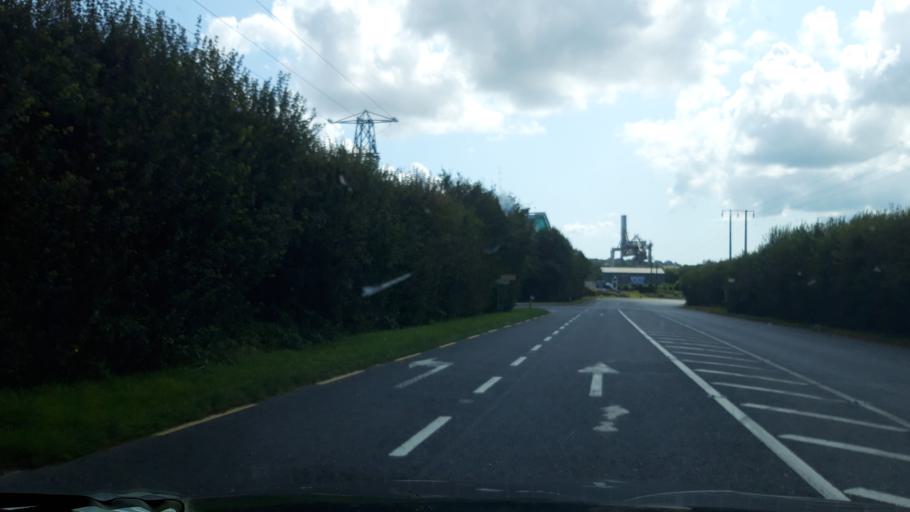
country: IE
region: Munster
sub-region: Waterford
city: Waterford
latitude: 52.2678
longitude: -7.0398
